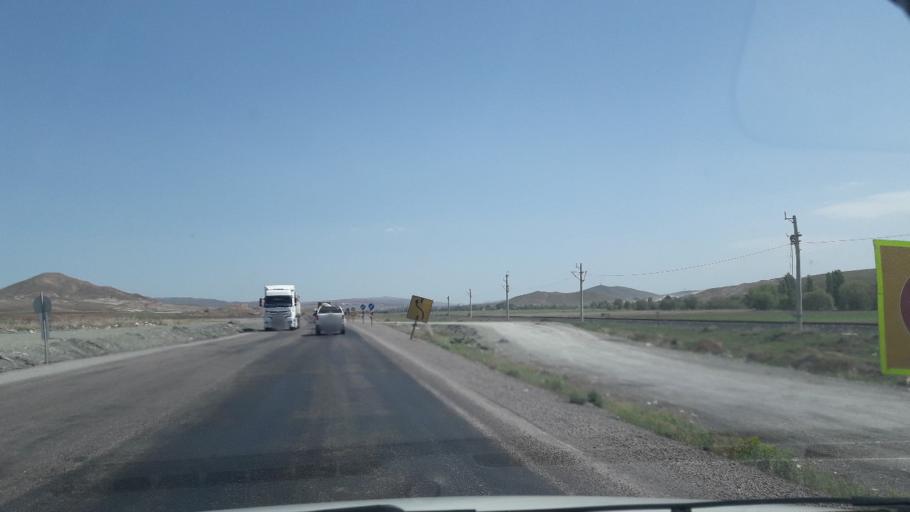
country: TR
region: Sivas
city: Ulas
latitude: 39.5252
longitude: 37.0119
